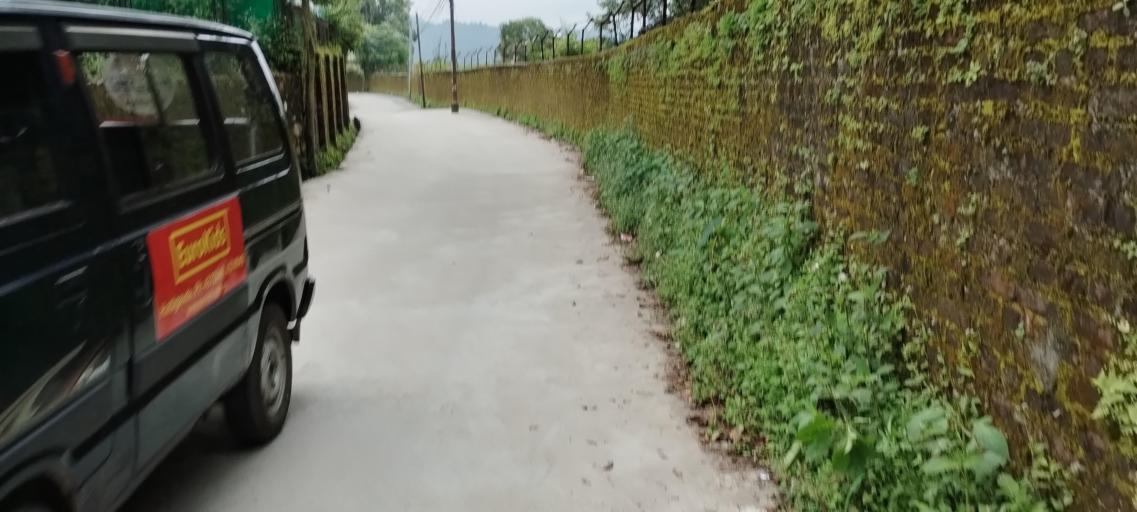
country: NP
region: Central Region
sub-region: Bagmati Zone
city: Kathmandu
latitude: 27.7832
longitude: 85.3625
